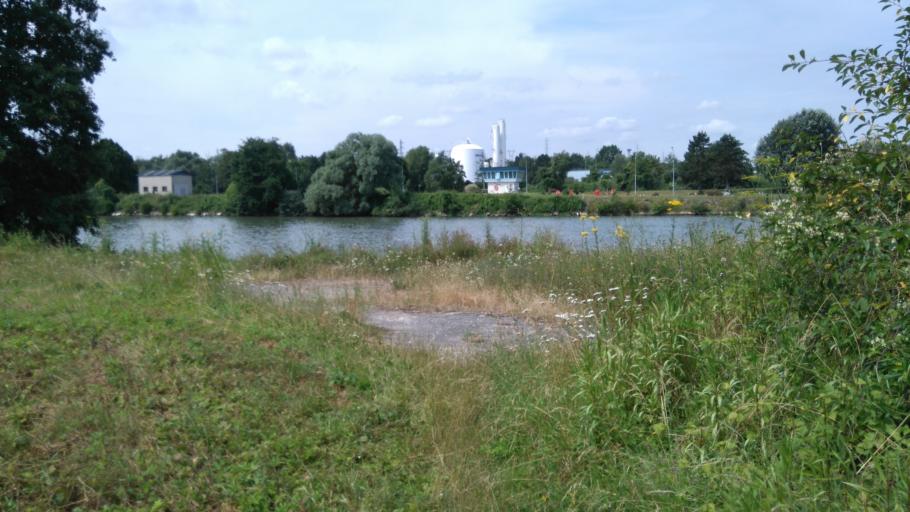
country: FR
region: Picardie
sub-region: Departement de l'Oise
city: Thiverny
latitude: 49.2437
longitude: 2.4540
